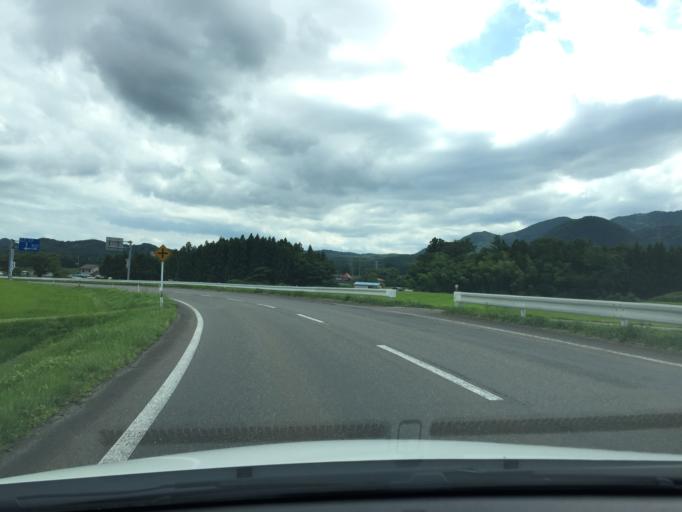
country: JP
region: Fukushima
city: Sukagawa
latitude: 37.2805
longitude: 140.1664
